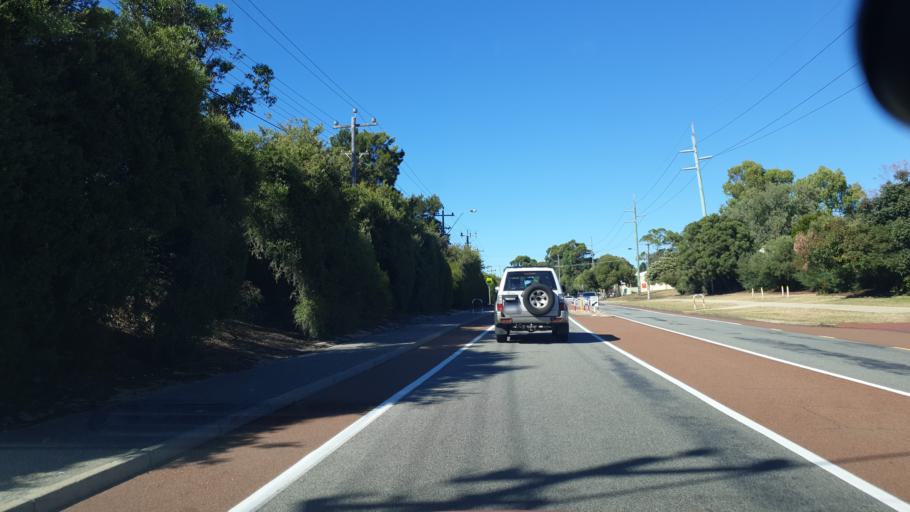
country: AU
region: Western Australia
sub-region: Melville
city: Mount Pleasant
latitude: -32.0506
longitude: 115.8587
